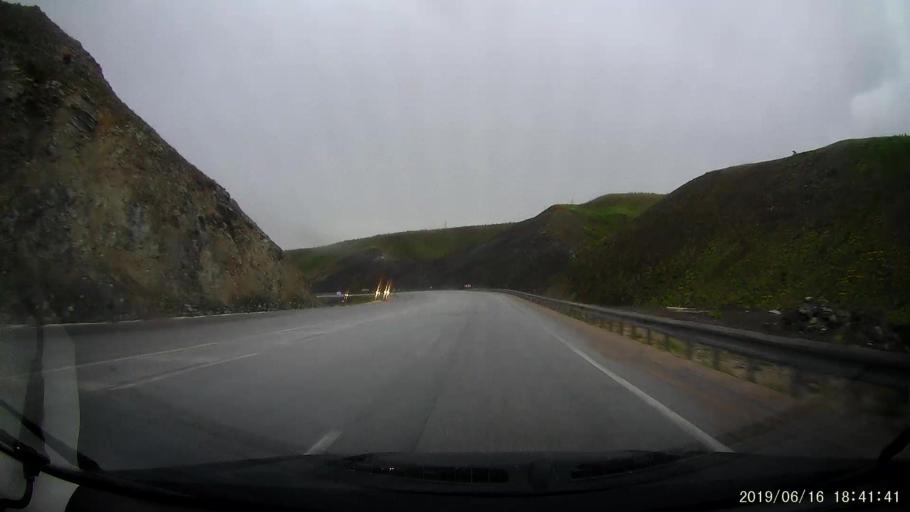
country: TR
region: Erzincan
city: Doganbeyli
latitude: 39.8724
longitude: 39.1241
